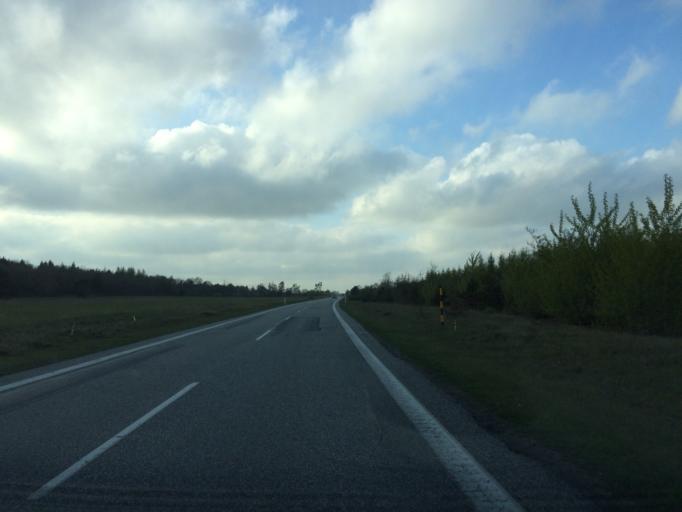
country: DK
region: Central Jutland
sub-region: Viborg Kommune
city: Karup
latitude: 56.3179
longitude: 9.1177
